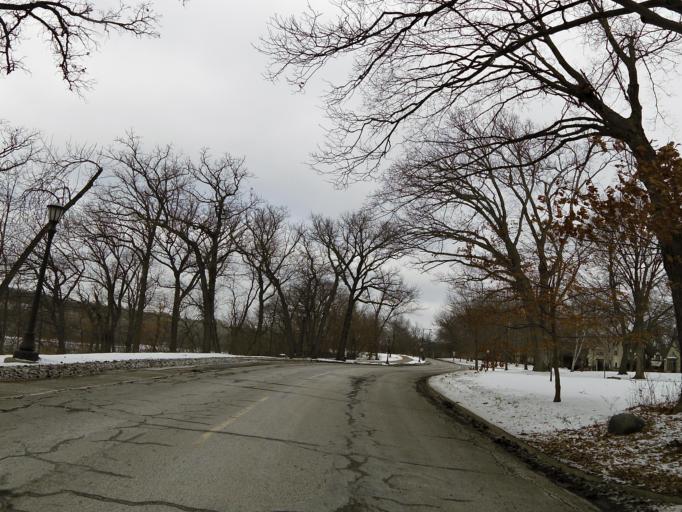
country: US
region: Minnesota
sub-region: Ramsey County
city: Lauderdale
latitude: 44.9332
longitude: -93.1985
